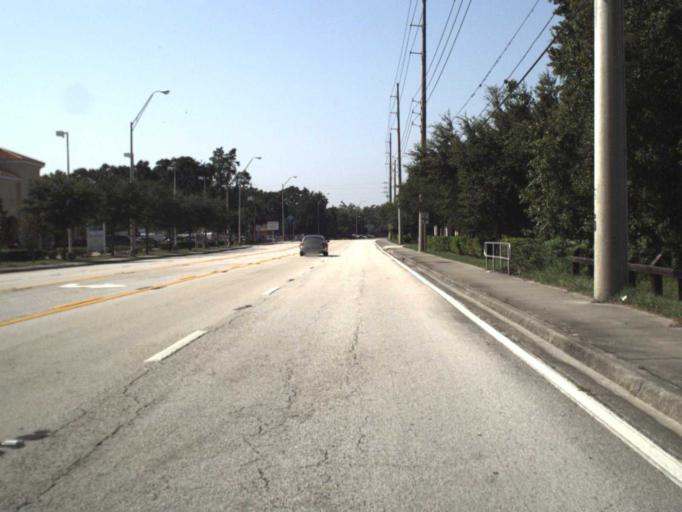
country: US
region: Florida
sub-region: Hillsborough County
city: Lake Magdalene
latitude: 28.1037
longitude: -82.4605
